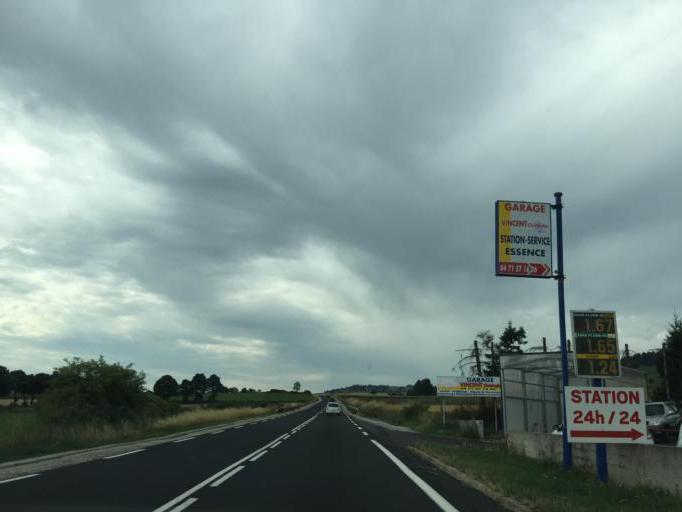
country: FR
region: Auvergne
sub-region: Departement de la Haute-Loire
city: Solignac-sur-Loire
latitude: 44.8885
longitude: 3.8478
